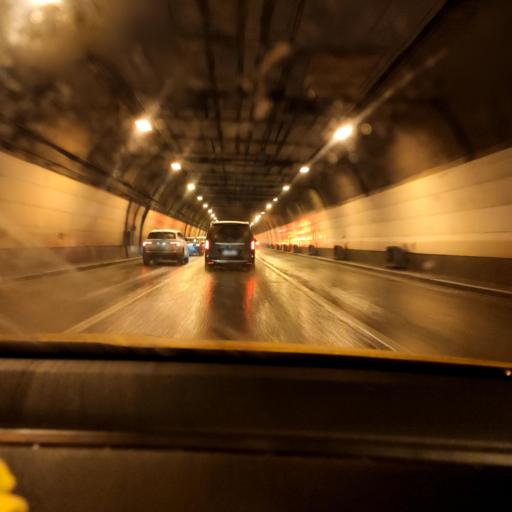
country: RU
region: Moscow
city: Rublevo
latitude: 55.7838
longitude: 37.3919
